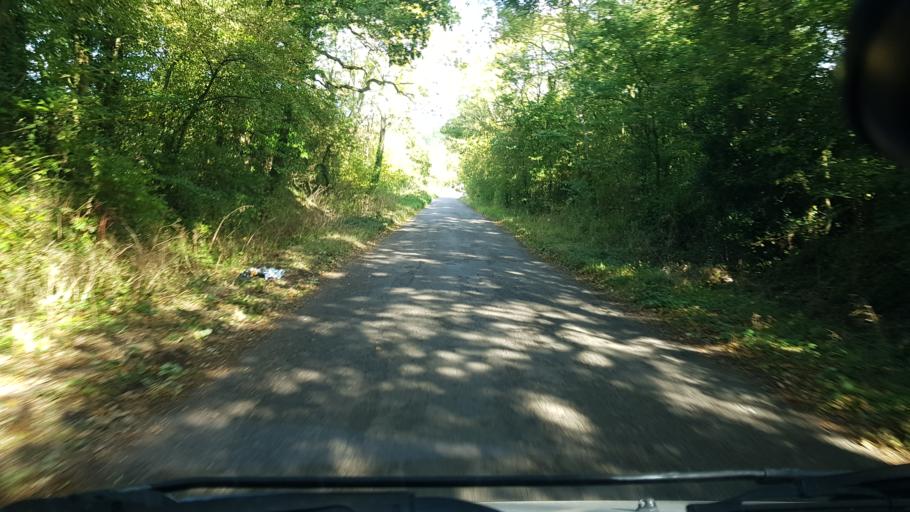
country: GB
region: England
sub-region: Surrey
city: Shalford
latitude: 51.2140
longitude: -0.5962
